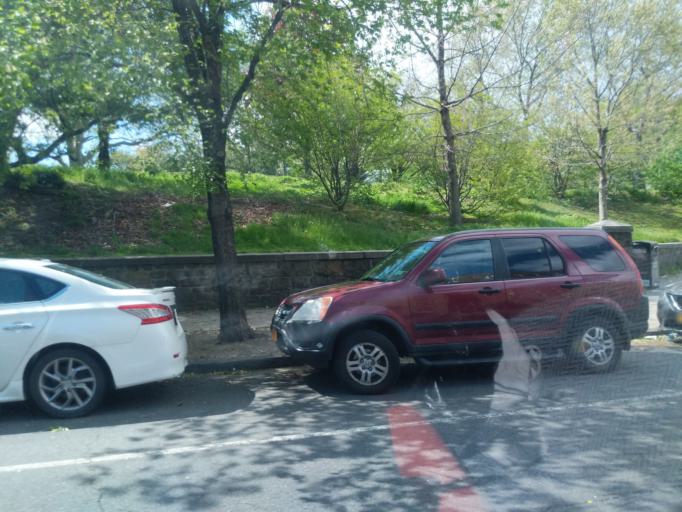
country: US
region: New York
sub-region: New York County
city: Inwood
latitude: 40.8247
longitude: -73.9240
